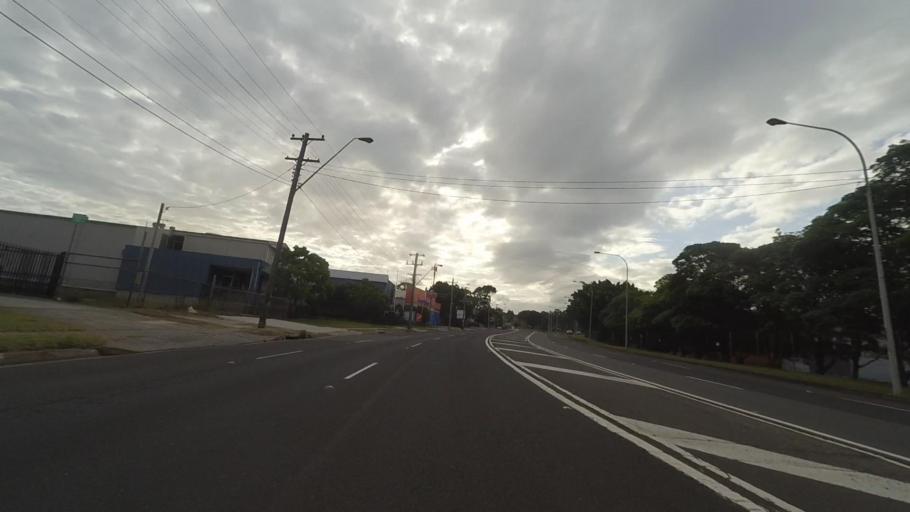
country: AU
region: New South Wales
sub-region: Wollongong
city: Port Kembla
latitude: -34.4785
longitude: 150.8900
